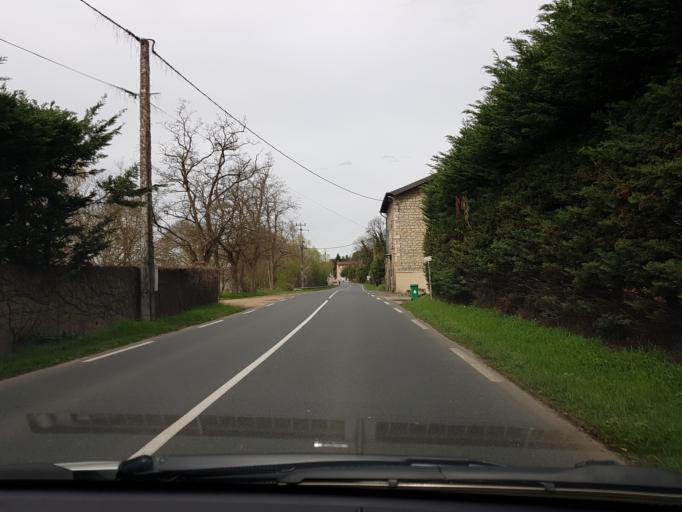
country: FR
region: Rhone-Alpes
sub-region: Departement de l'Ain
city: Jassans-Riottier
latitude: 45.9662
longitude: 4.7539
